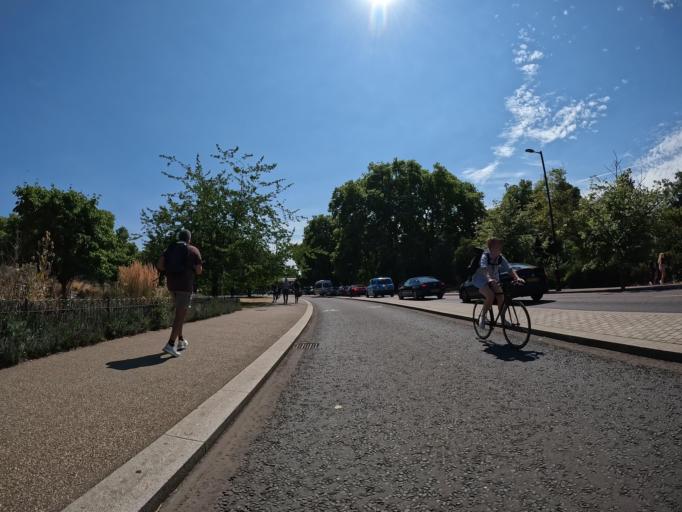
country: GB
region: England
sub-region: Greater London
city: Bayswater
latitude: 51.5034
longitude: -0.1743
